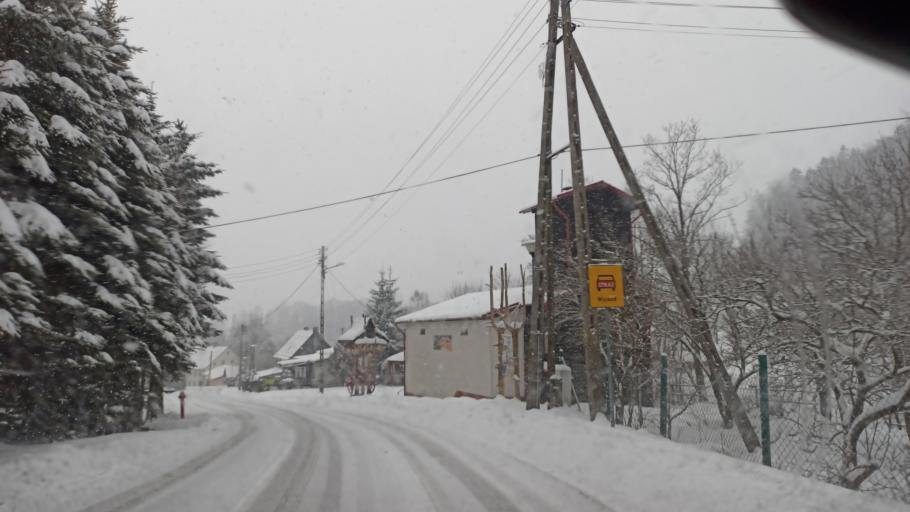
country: PL
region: Lower Silesian Voivodeship
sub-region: Powiat klodzki
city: Ludwikowice Klodzkie
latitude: 50.6546
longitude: 16.4729
